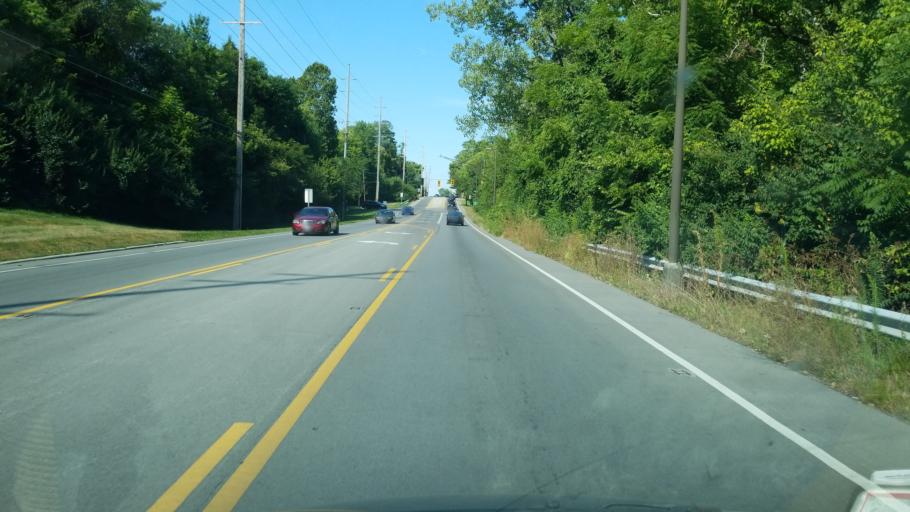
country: US
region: Ohio
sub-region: Franklin County
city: Dublin
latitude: 40.0661
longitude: -83.1199
